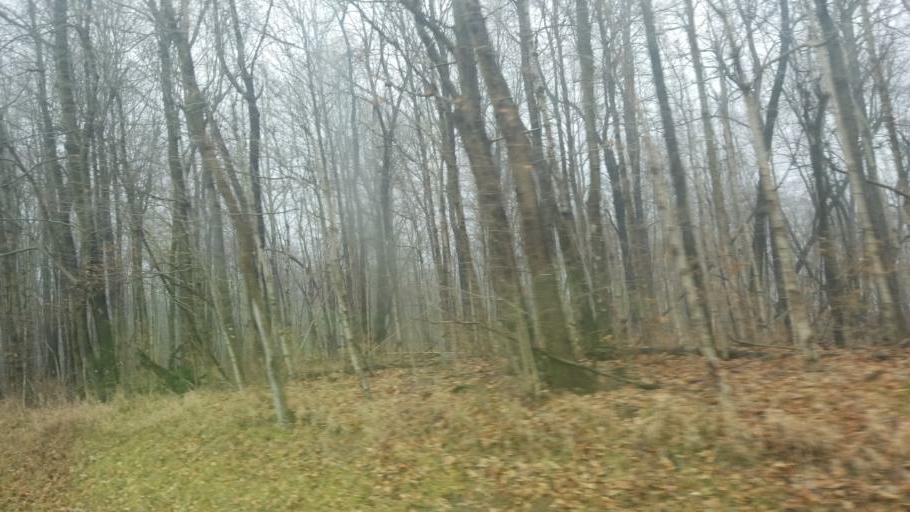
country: US
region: Ohio
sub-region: Champaign County
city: North Lewisburg
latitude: 40.2885
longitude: -83.6230
